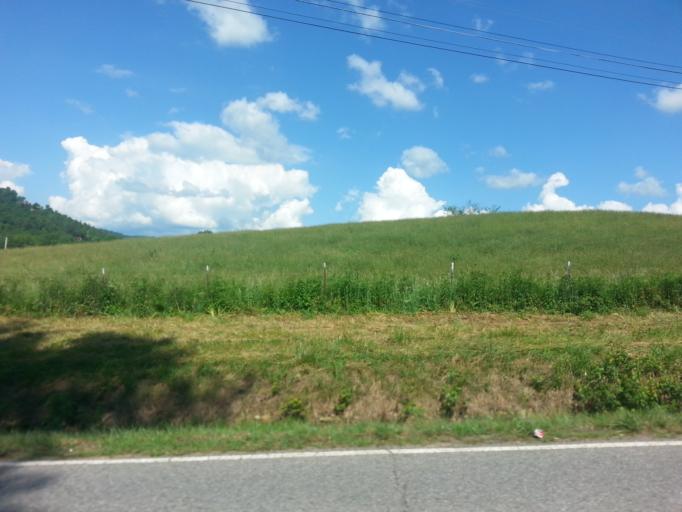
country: US
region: Georgia
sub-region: Towns County
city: Hiawassee
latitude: 34.9181
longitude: -83.7293
